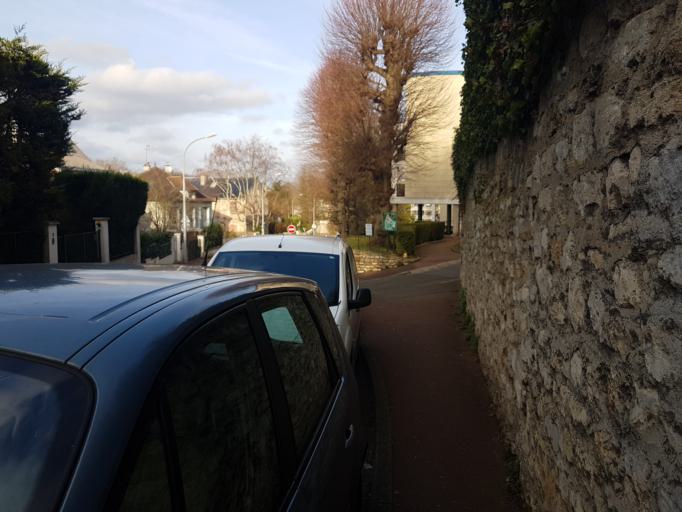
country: FR
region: Ile-de-France
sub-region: Departement des Yvelines
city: Louveciennes
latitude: 48.8621
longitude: 2.1141
